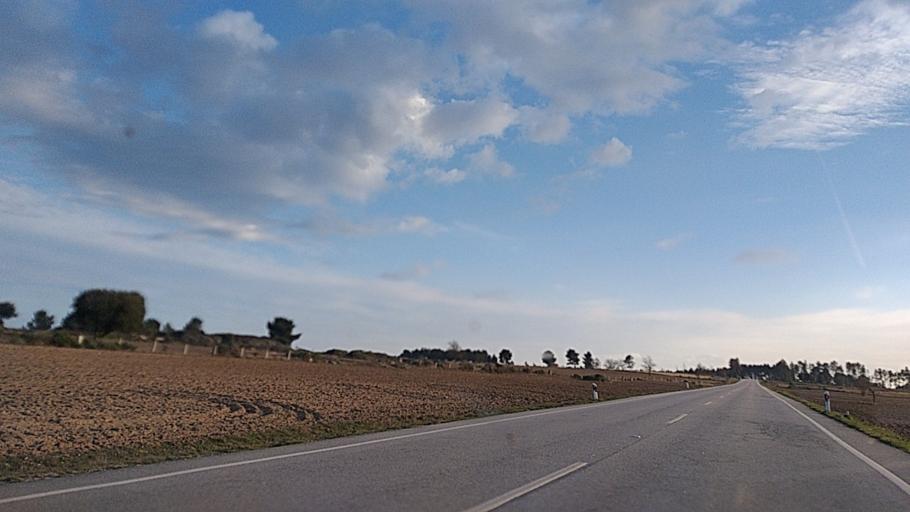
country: PT
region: Guarda
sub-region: Pinhel
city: Pinhel
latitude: 40.6490
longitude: -6.9677
